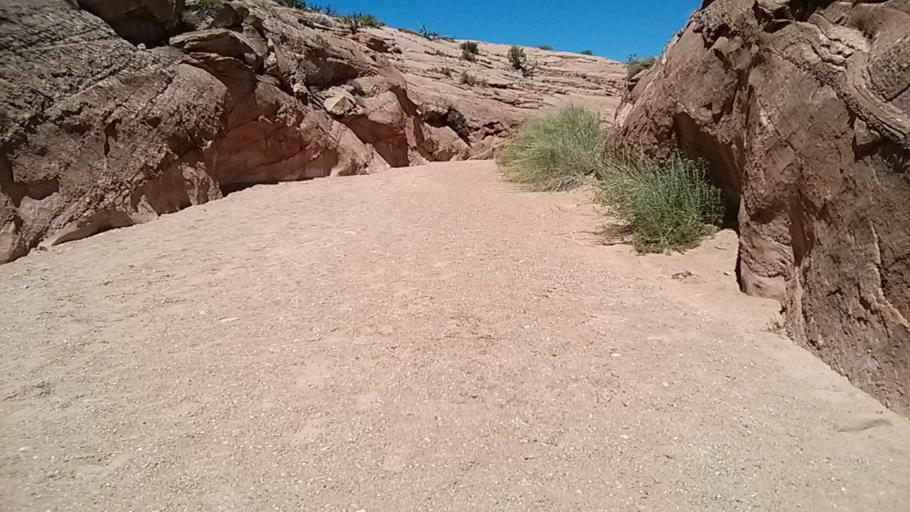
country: US
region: Arizona
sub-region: Coconino County
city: Page
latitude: 37.4792
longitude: -111.2115
